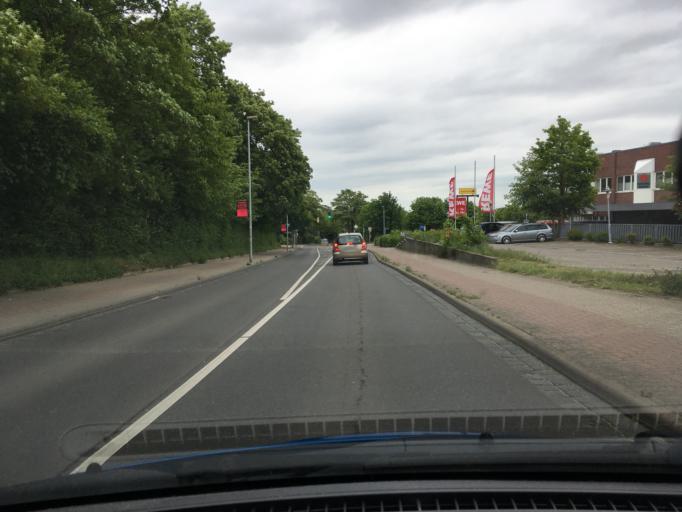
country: DE
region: Mecklenburg-Vorpommern
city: Wismar
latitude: 53.8877
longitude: 11.4371
